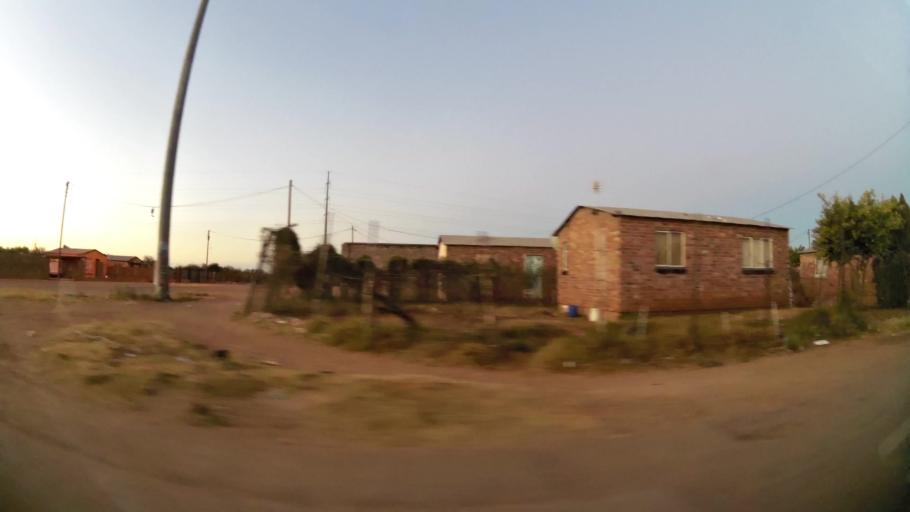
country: ZA
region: Northern Cape
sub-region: Frances Baard District Municipality
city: Kimberley
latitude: -28.7122
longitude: 24.7574
